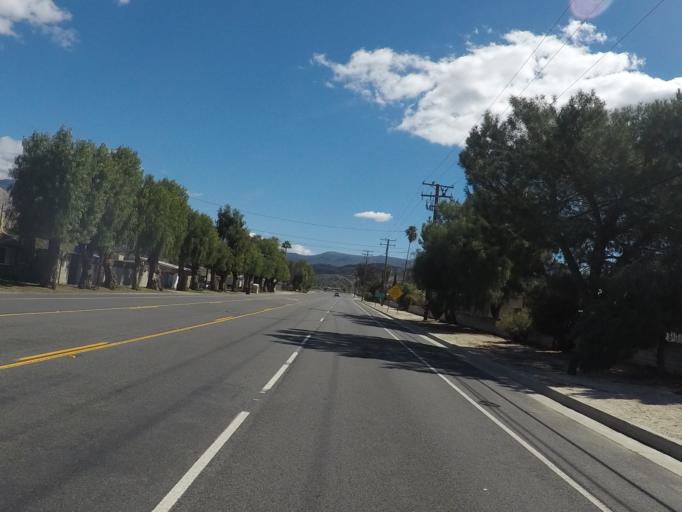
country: US
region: California
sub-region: Riverside County
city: Valle Vista
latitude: 33.7451
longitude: -116.8649
